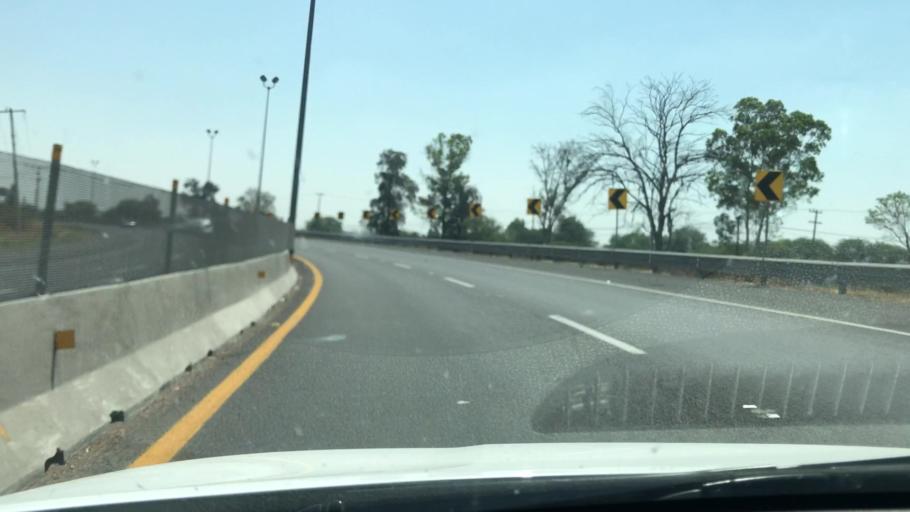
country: MX
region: Guanajuato
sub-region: Abasolo
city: San Bernardo Pena Blanca
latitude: 20.4659
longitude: -101.5088
